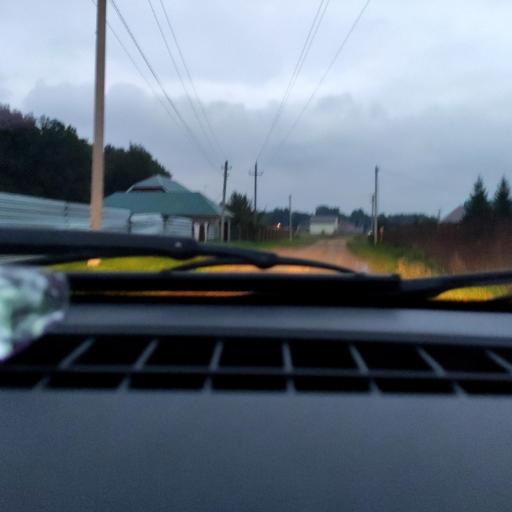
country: RU
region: Bashkortostan
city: Iglino
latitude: 54.7330
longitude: 56.3276
